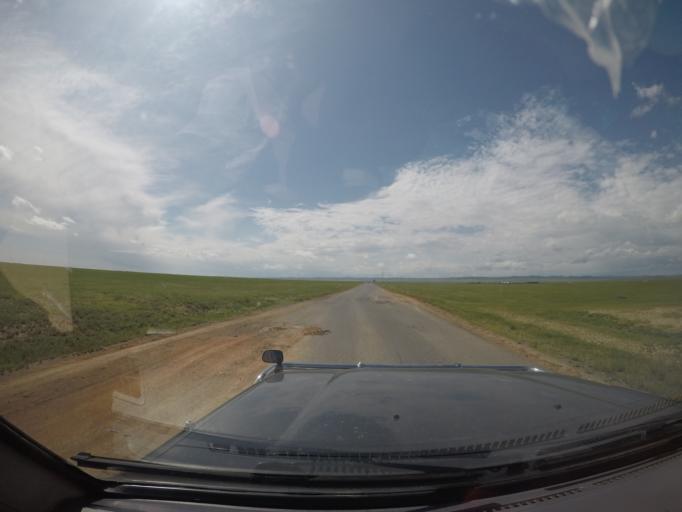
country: MN
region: Hentiy
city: Moron
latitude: 47.4217
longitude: 110.0901
